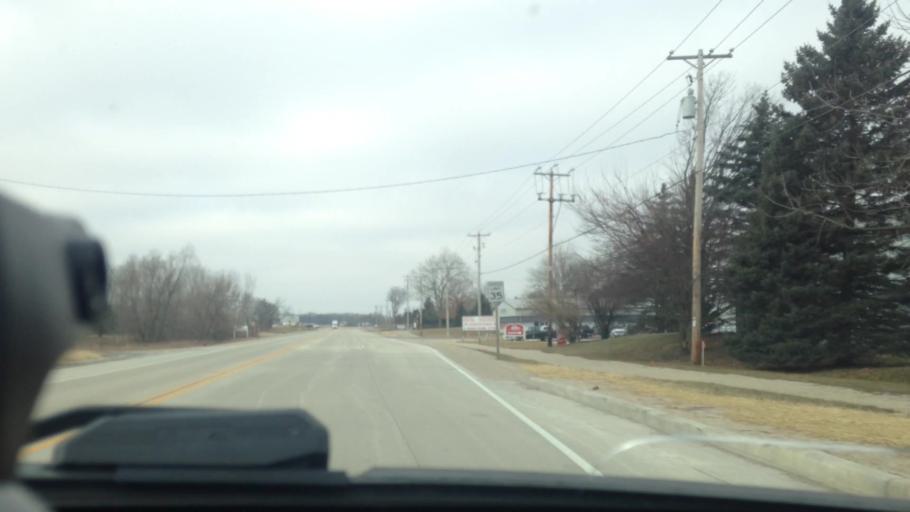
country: US
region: Wisconsin
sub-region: Dodge County
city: Horicon
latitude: 43.4534
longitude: -88.6484
